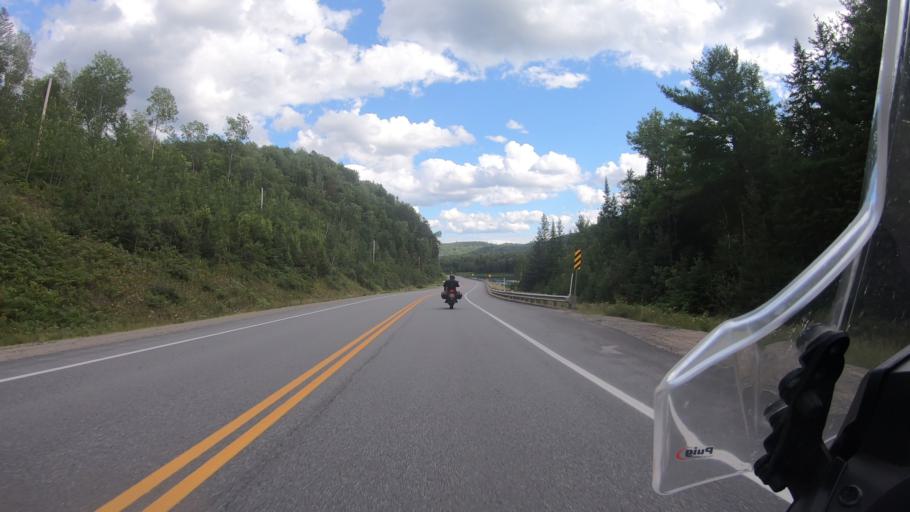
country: CA
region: Quebec
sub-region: Mauricie
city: Saint-Tite
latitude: 47.0017
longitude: -72.9248
